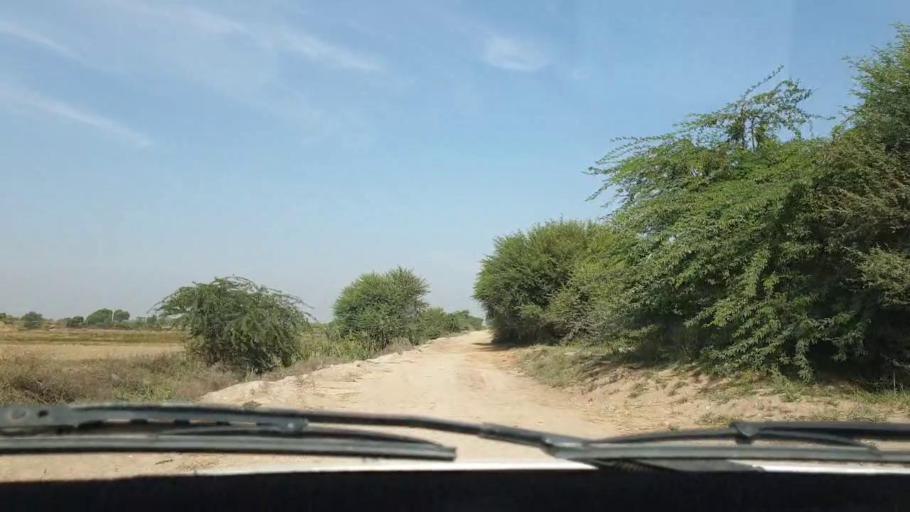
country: PK
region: Sindh
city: Bulri
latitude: 24.8970
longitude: 68.4624
